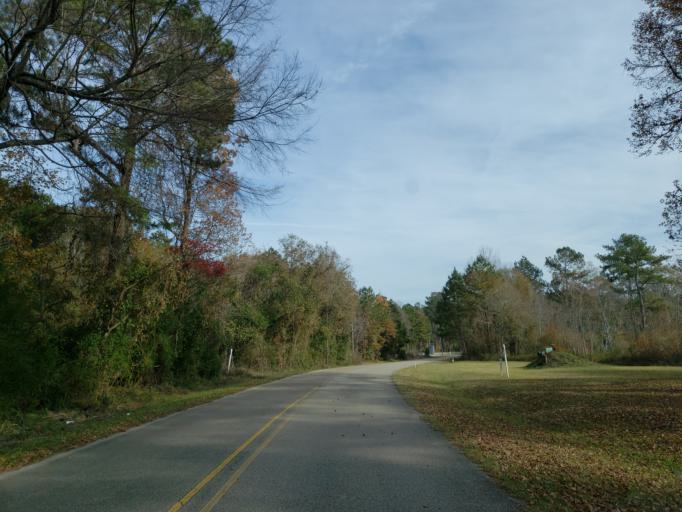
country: US
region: Mississippi
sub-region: Forrest County
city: Glendale
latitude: 31.3536
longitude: -89.3298
